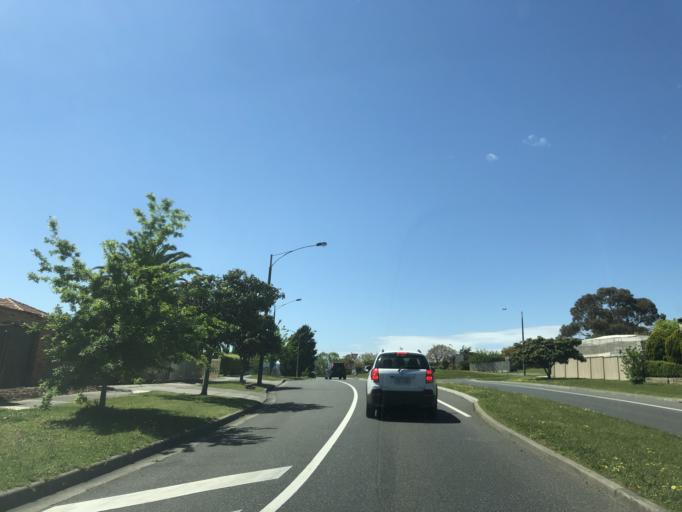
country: AU
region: Victoria
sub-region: Casey
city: Endeavour Hills
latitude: -37.9729
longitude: 145.2599
